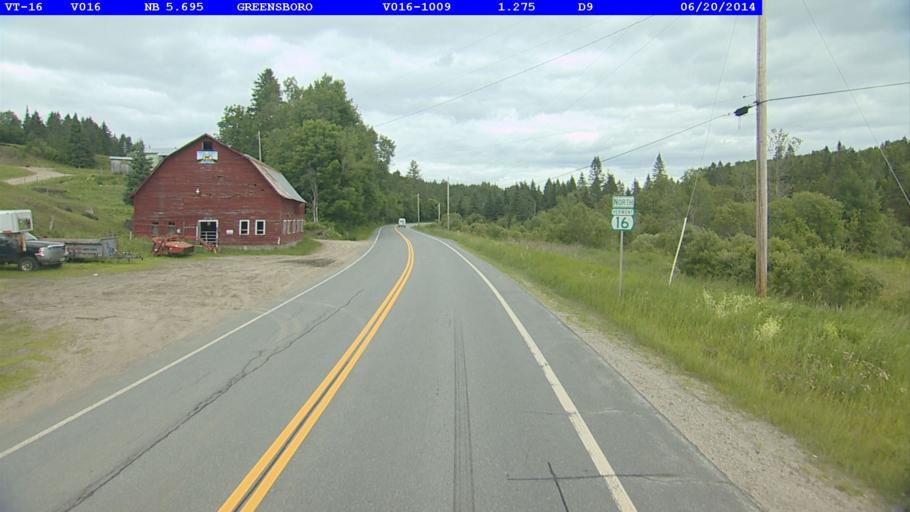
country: US
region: Vermont
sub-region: Caledonia County
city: Hardwick
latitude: 44.5608
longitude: -72.2570
